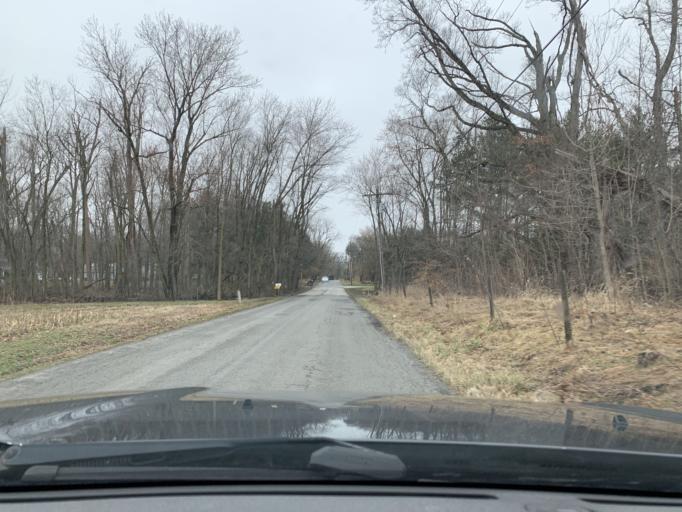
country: US
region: Indiana
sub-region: Porter County
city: Chesterton
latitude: 41.6070
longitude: -86.9991
